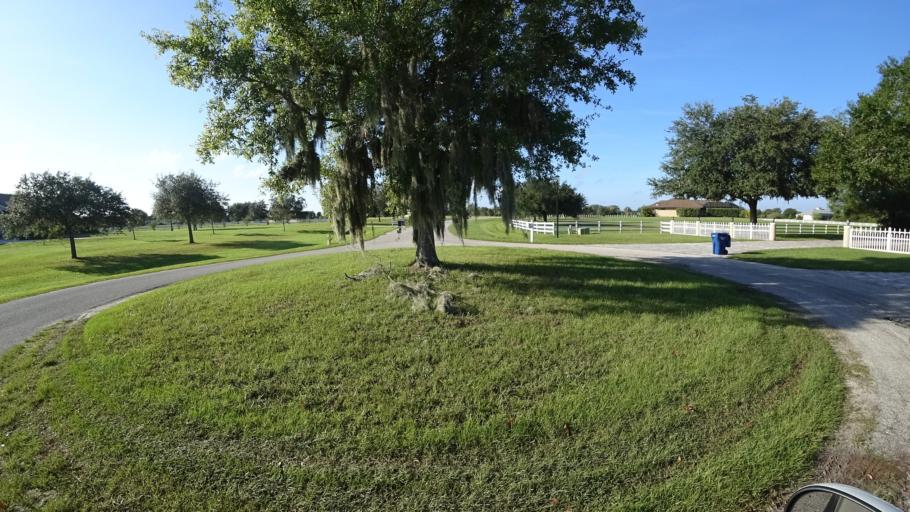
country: US
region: Florida
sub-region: Hillsborough County
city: Sun City Center
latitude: 27.5591
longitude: -82.3534
